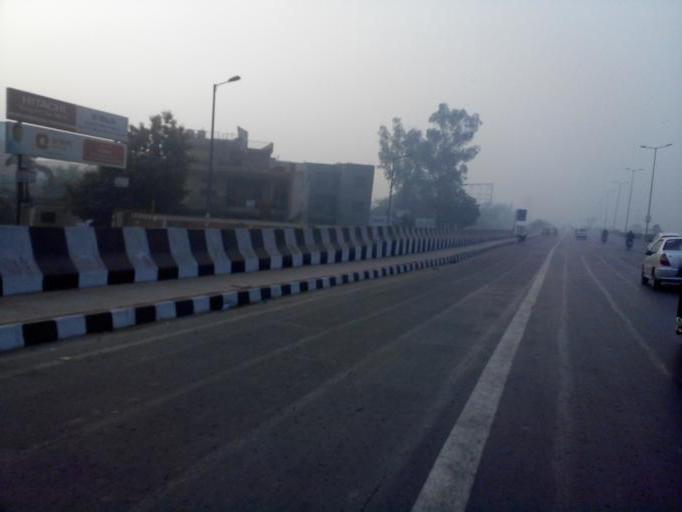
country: IN
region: Uttar Pradesh
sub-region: Gautam Buddha Nagar
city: Noida
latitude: 28.6582
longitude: 77.3200
